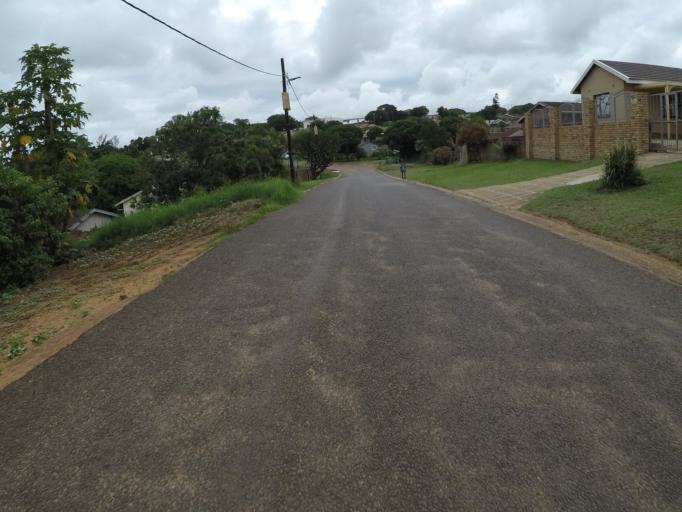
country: ZA
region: KwaZulu-Natal
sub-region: uThungulu District Municipality
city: Empangeni
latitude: -28.7724
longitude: 31.8660
